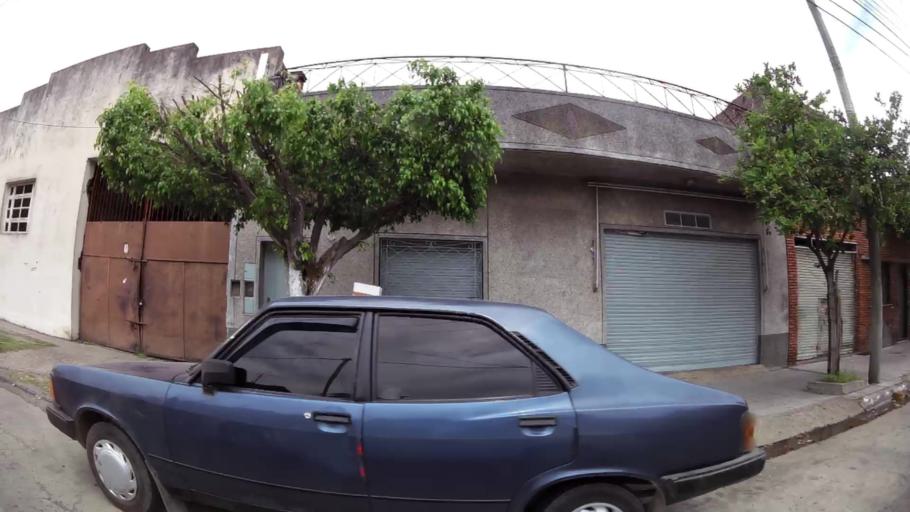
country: AR
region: Buenos Aires
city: San Justo
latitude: -34.6747
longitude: -58.5403
